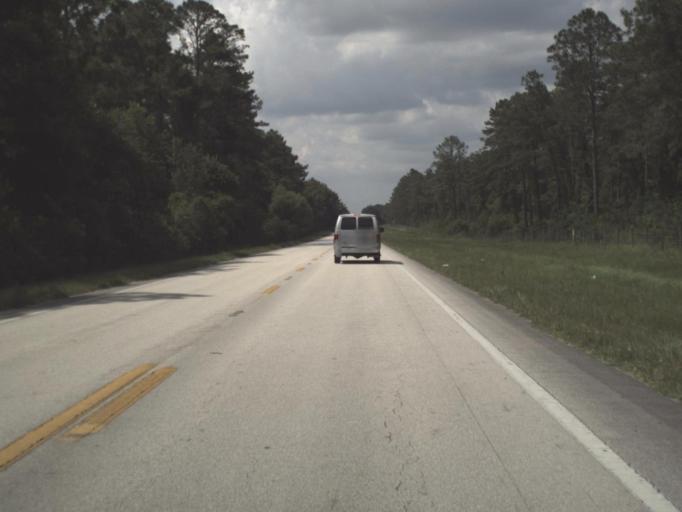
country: US
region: Florida
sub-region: Bradford County
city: Starke
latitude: 29.9460
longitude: -82.0162
